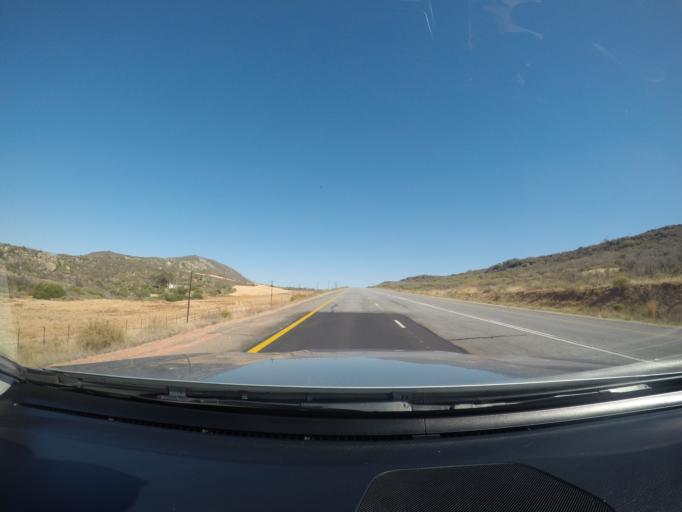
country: ZA
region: Western Cape
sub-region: West Coast District Municipality
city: Clanwilliam
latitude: -32.2983
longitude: 18.9020
